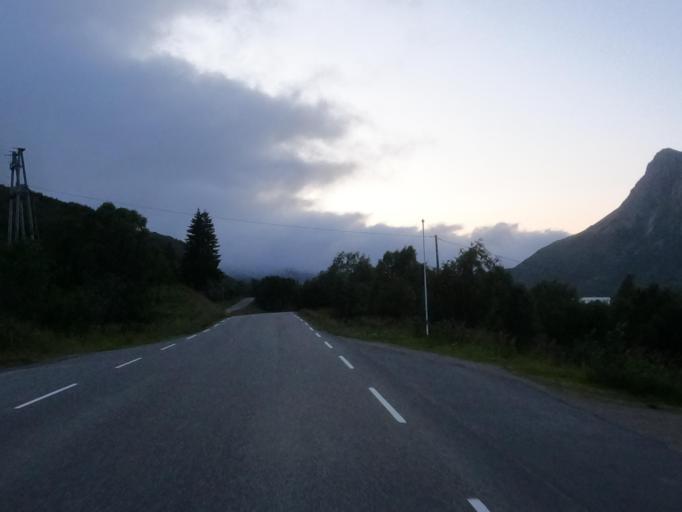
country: NO
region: Nordland
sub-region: Lodingen
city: Lodingen
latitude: 68.5845
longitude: 15.7918
